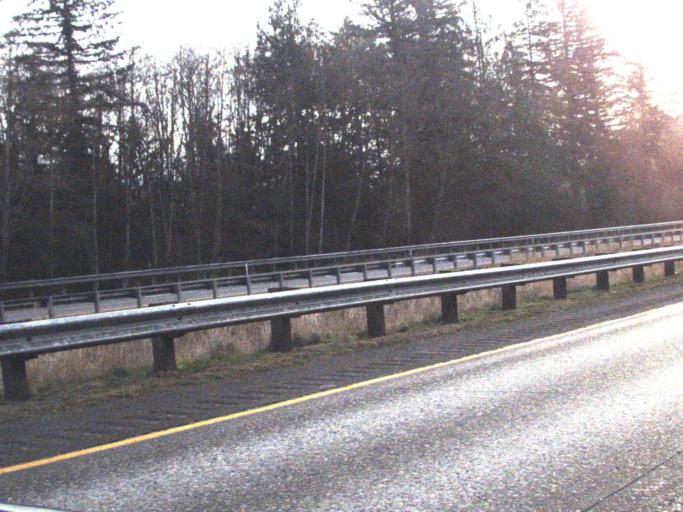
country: US
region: Washington
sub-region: Whatcom County
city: Sudden Valley
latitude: 48.6080
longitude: -122.3473
